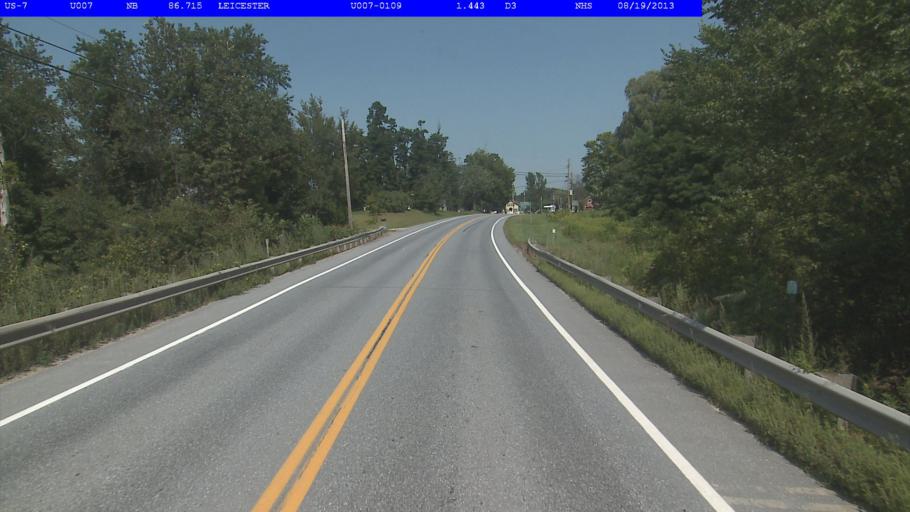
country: US
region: Vermont
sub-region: Rutland County
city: Brandon
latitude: 43.8641
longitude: -73.1074
